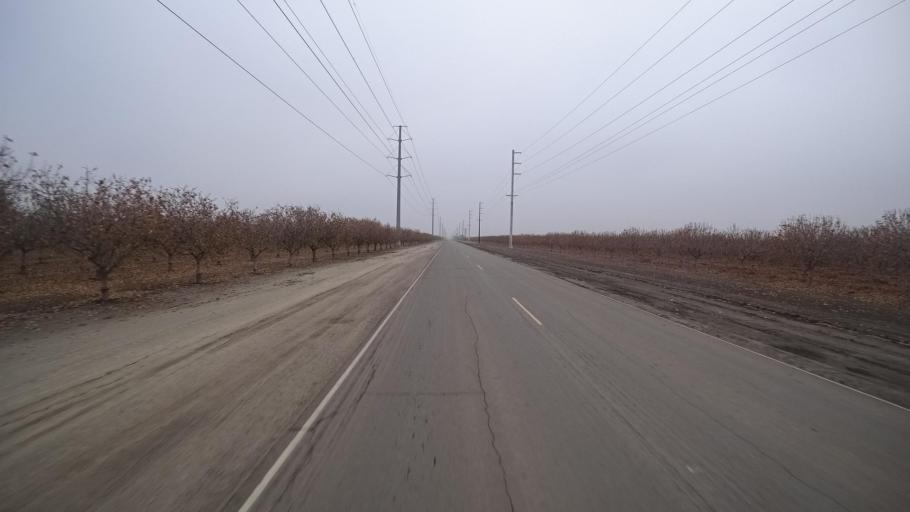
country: US
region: California
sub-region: Kern County
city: Buttonwillow
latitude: 35.3719
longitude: -119.4476
